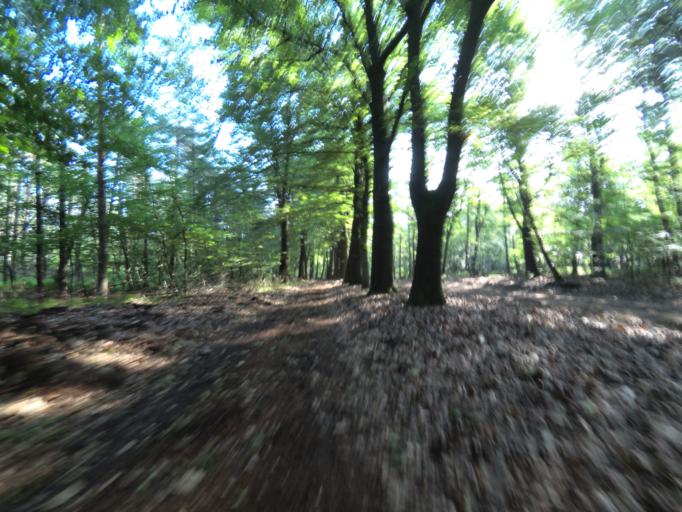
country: NL
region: Gelderland
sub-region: Gemeente Apeldoorn
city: Beekbergen
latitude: 52.1686
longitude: 5.8704
